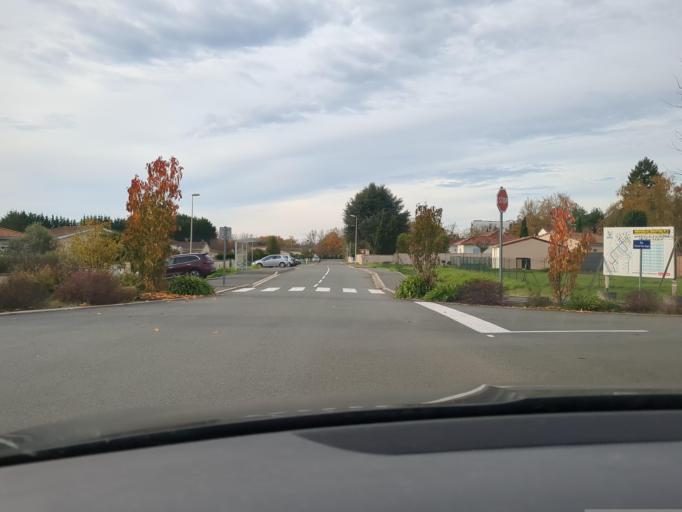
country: FR
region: Poitou-Charentes
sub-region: Departement de la Charente-Maritime
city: Jonzac
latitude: 45.4527
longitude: -0.4451
